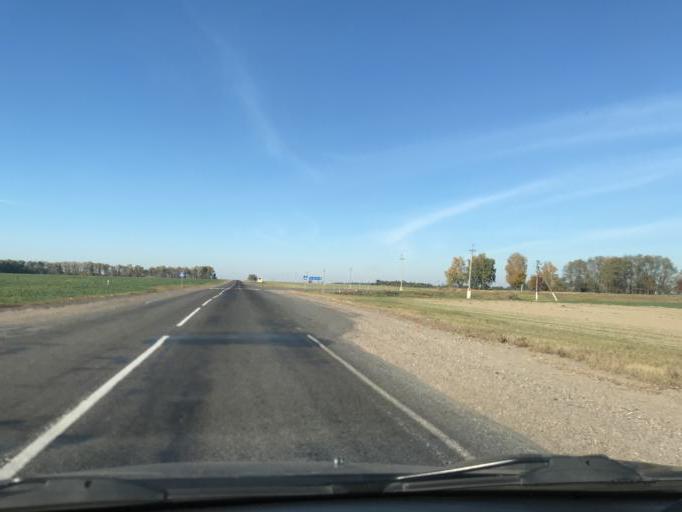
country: BY
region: Gomel
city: Brahin
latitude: 51.7965
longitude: 30.1482
